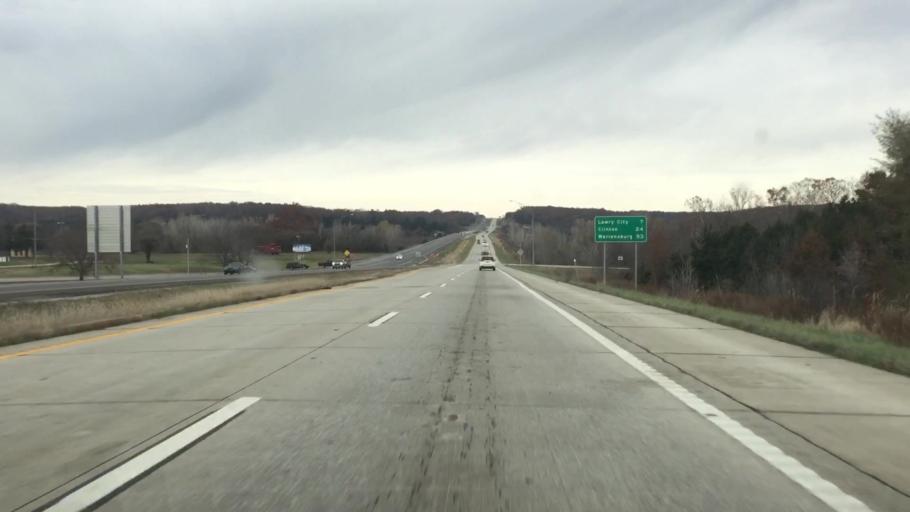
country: US
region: Missouri
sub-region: Saint Clair County
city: Osceola
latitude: 38.0521
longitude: -93.6879
